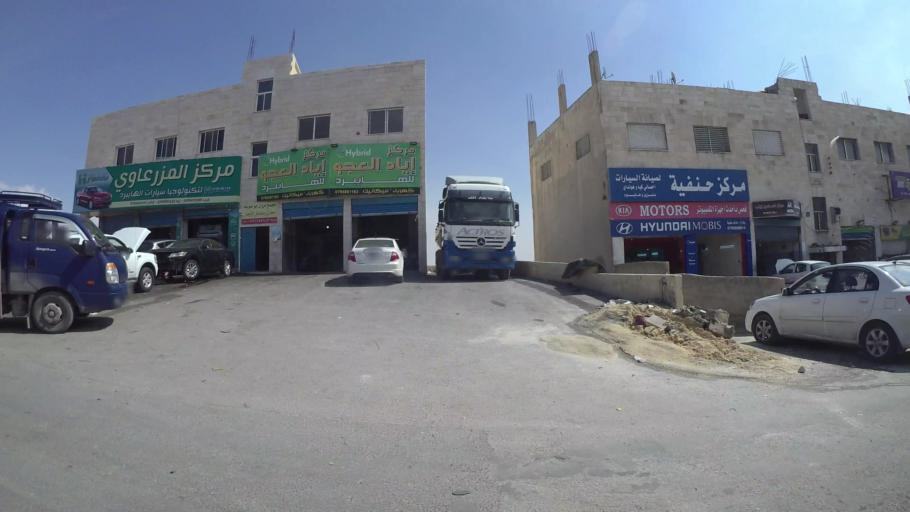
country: JO
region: Zarqa
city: Russeifa
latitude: 31.9898
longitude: 36.0036
